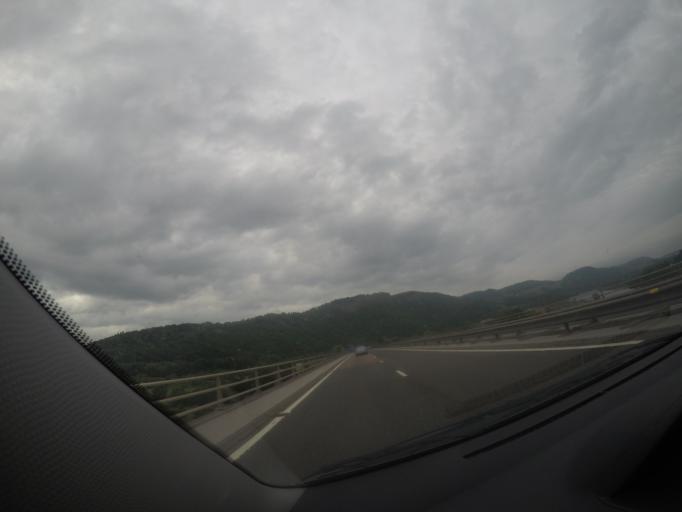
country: GB
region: Scotland
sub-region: Perth and Kinross
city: Perth
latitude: 56.3785
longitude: -3.4100
